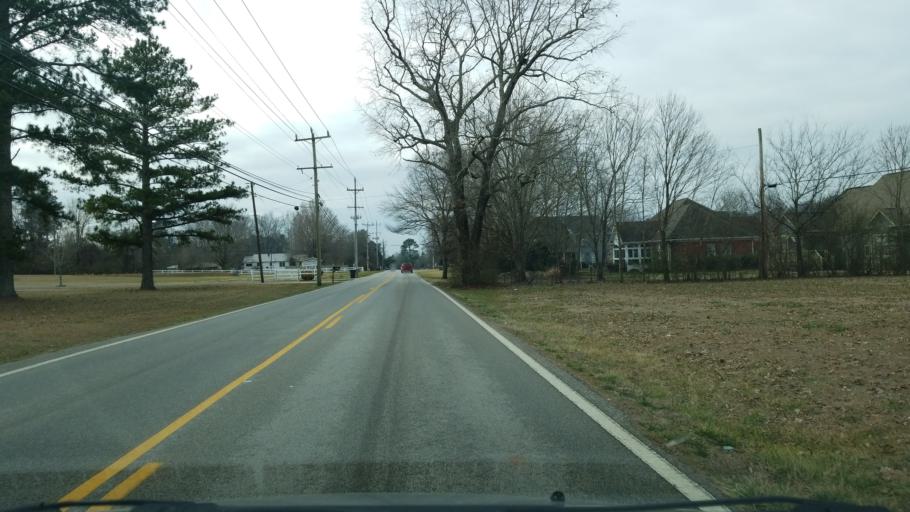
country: US
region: Tennessee
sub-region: Hamilton County
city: Collegedale
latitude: 35.0325
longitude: -85.0808
